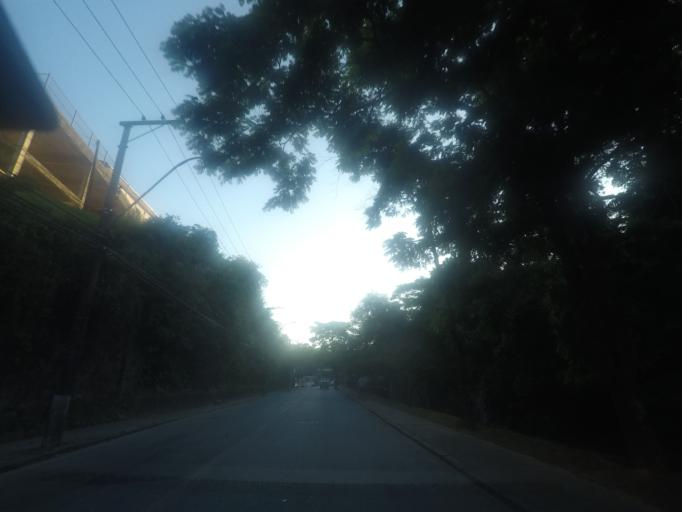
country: BR
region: Rio de Janeiro
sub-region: Petropolis
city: Petropolis
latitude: -22.5314
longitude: -43.1991
